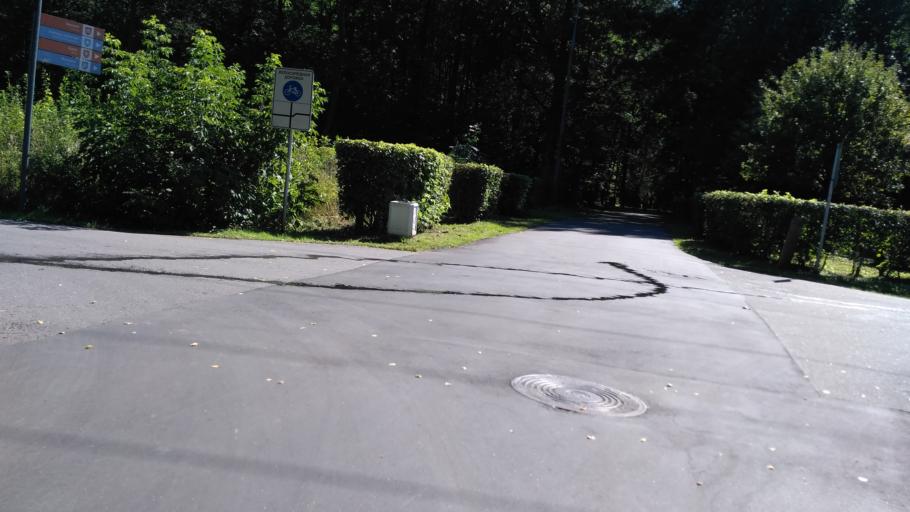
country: RU
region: Moscow
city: Metrogorodok
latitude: 55.7804
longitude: 37.7529
